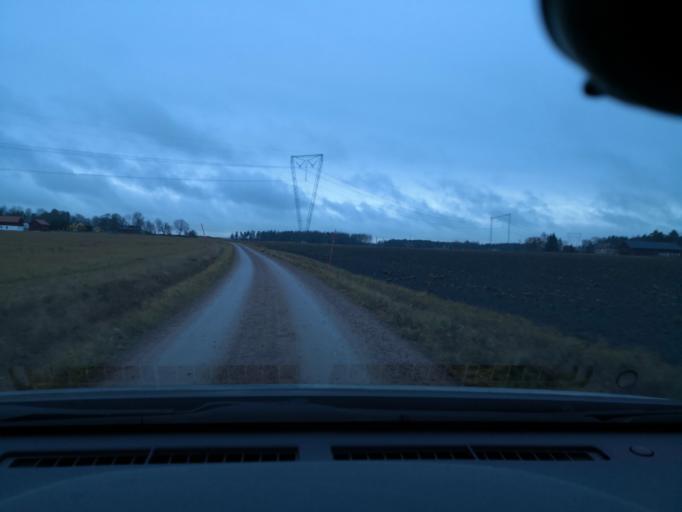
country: SE
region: Vaestmanland
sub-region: Hallstahammars Kommun
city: Kolback
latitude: 59.5651
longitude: 16.1852
